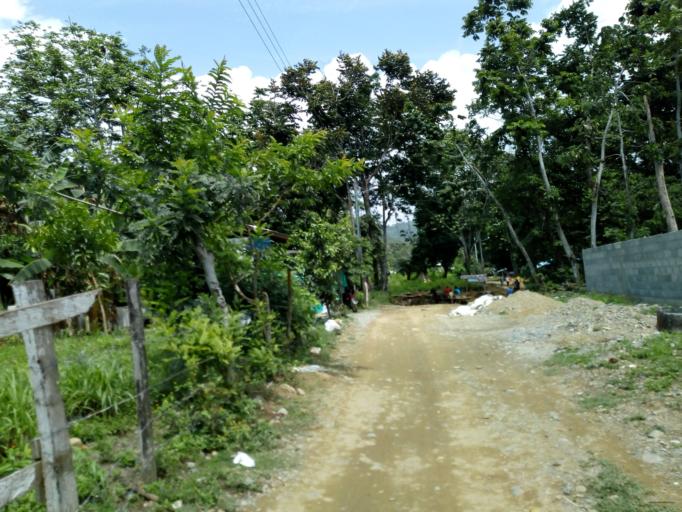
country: PA
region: Guna Yala
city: Puerto Obaldia
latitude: 8.6281
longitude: -77.3541
